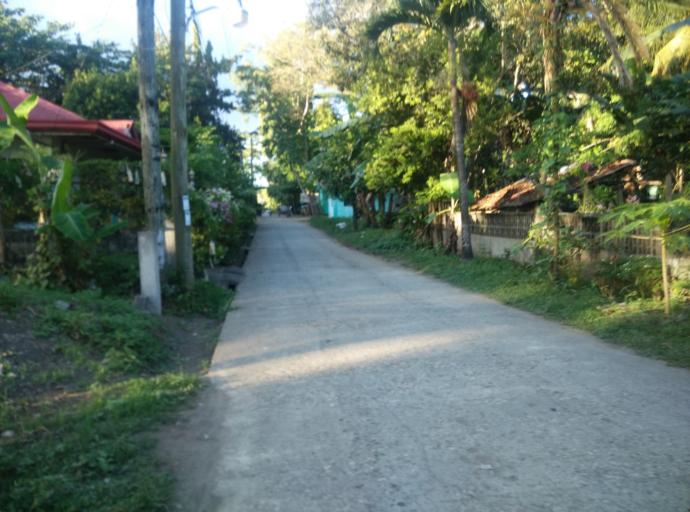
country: PH
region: Eastern Visayas
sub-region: Province of Leyte
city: Matalom
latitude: 10.2815
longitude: 124.7849
